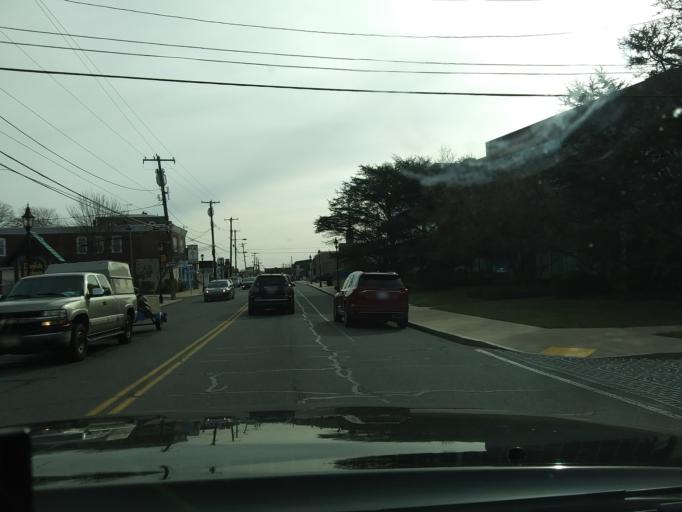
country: US
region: Pennsylvania
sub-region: Montgomery County
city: Rockledge
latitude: 40.0794
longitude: -75.0878
